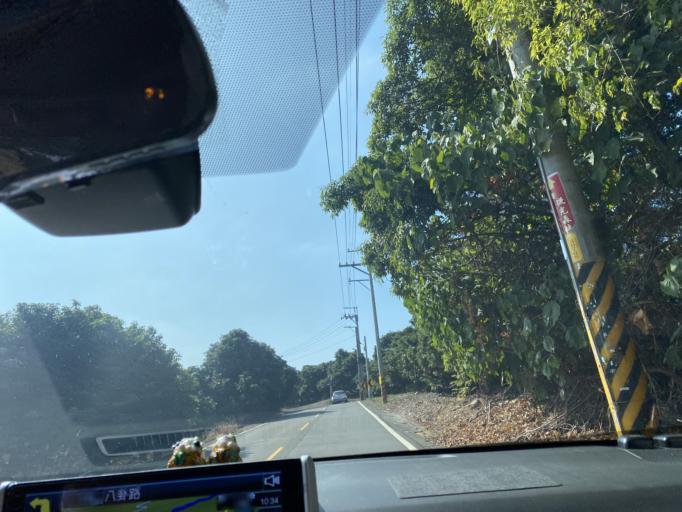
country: TW
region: Taiwan
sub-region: Nantou
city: Nantou
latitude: 23.9407
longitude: 120.6498
